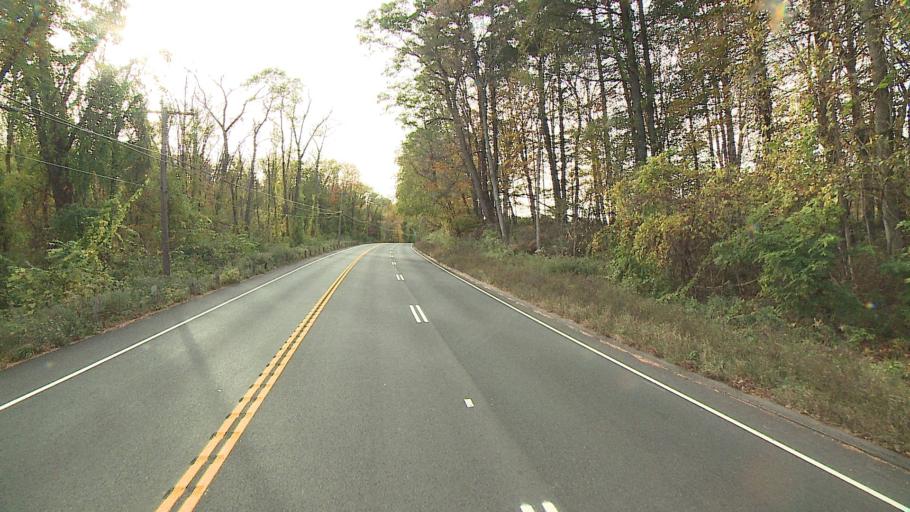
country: US
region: Connecticut
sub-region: Litchfield County
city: Canaan
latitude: 42.0037
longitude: -73.3736
